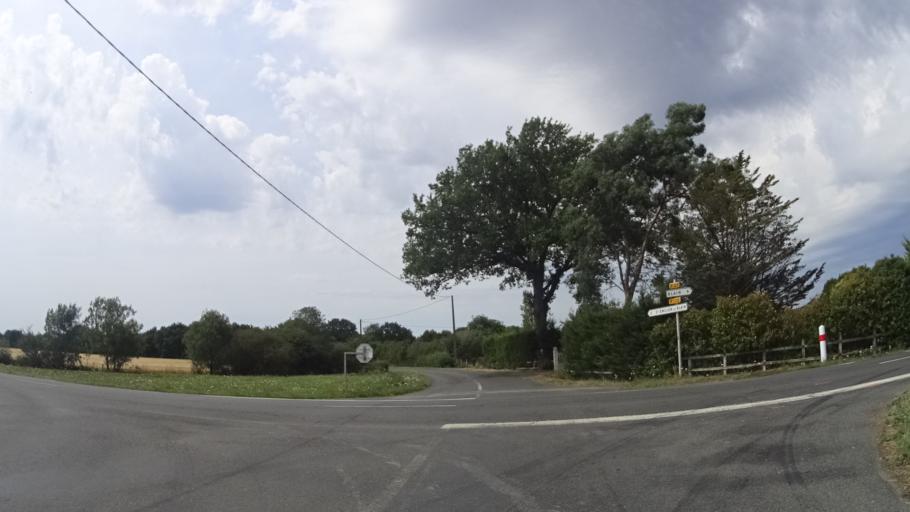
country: FR
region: Pays de la Loire
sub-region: Departement de la Loire-Atlantique
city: Heric
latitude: 47.4568
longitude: -1.6922
